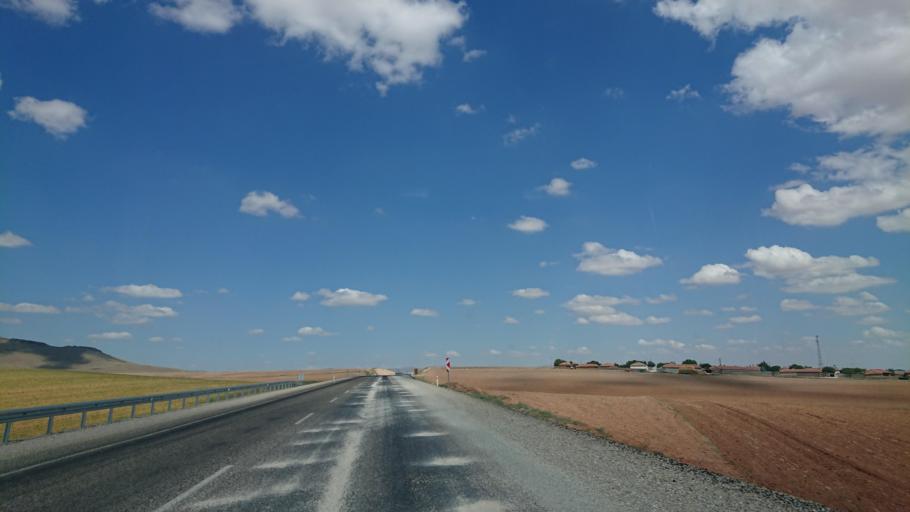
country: TR
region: Kirsehir
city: Kirsehir
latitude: 39.1237
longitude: 33.9807
